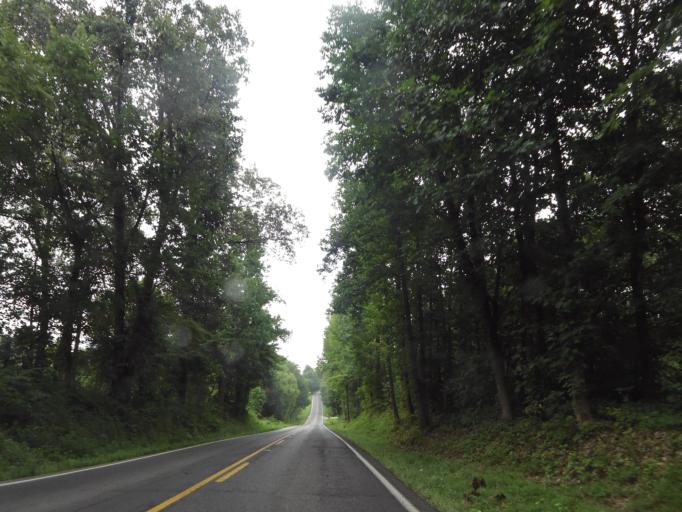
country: US
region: Kentucky
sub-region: Ballard County
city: Wickliffe
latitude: 36.9748
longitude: -89.0476
